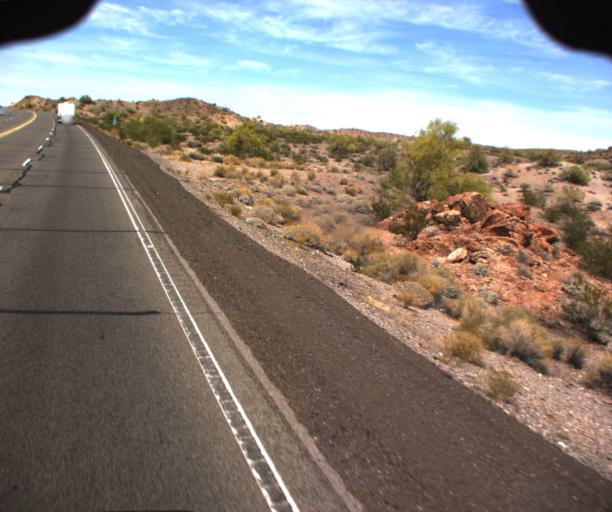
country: US
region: Arizona
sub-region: Mohave County
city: Desert Hills
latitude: 34.6333
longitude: -114.3264
